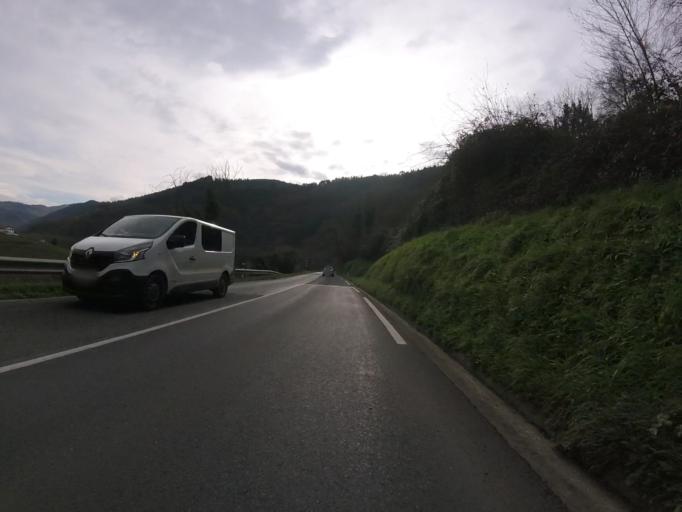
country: ES
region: Basque Country
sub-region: Provincia de Guipuzcoa
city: Cestona
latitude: 43.2556
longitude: -2.2556
